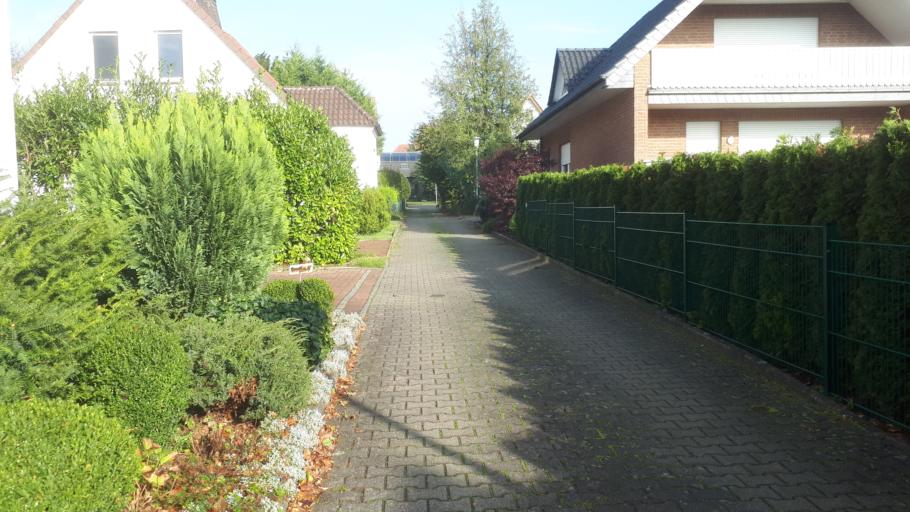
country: DE
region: North Rhine-Westphalia
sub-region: Regierungsbezirk Detmold
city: Huellhorst
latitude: 52.2737
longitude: 8.7082
